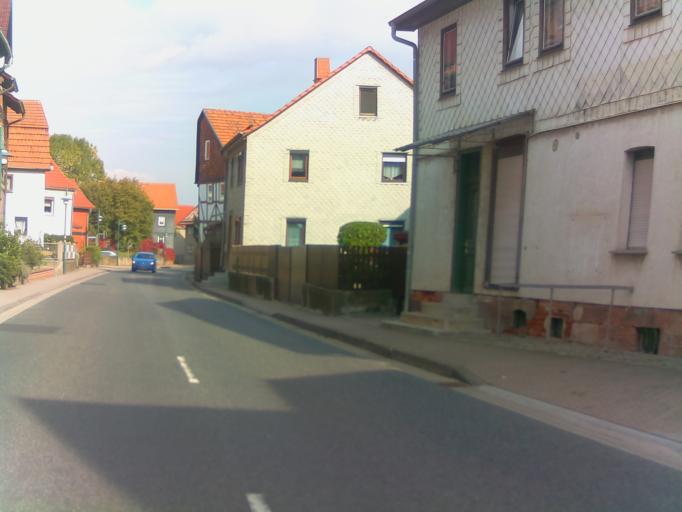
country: DE
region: Thuringia
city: Gerstungen
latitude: 50.9656
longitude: 10.0713
